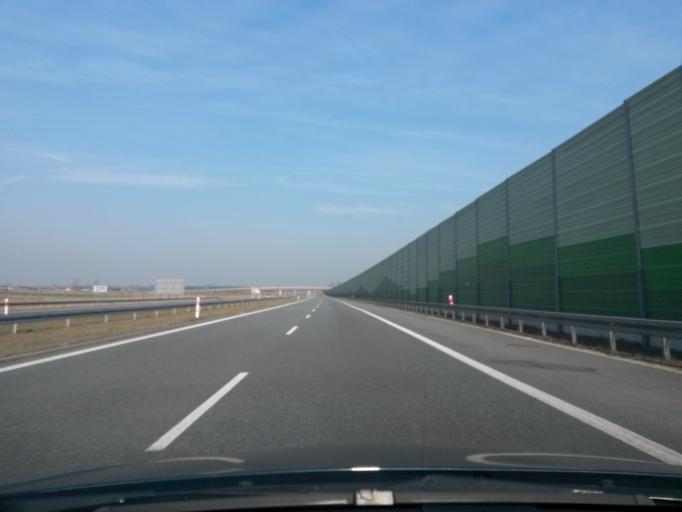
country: PL
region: Lodz Voivodeship
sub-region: Powiat leczycki
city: Piatek
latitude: 52.0795
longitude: 19.5304
